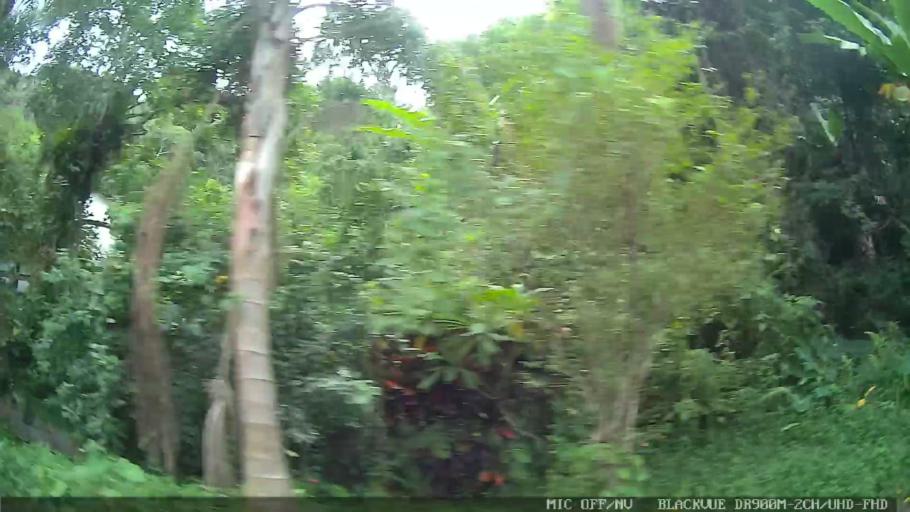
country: BR
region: Sao Paulo
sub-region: Iguape
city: Iguape
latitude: -24.7008
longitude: -47.5383
